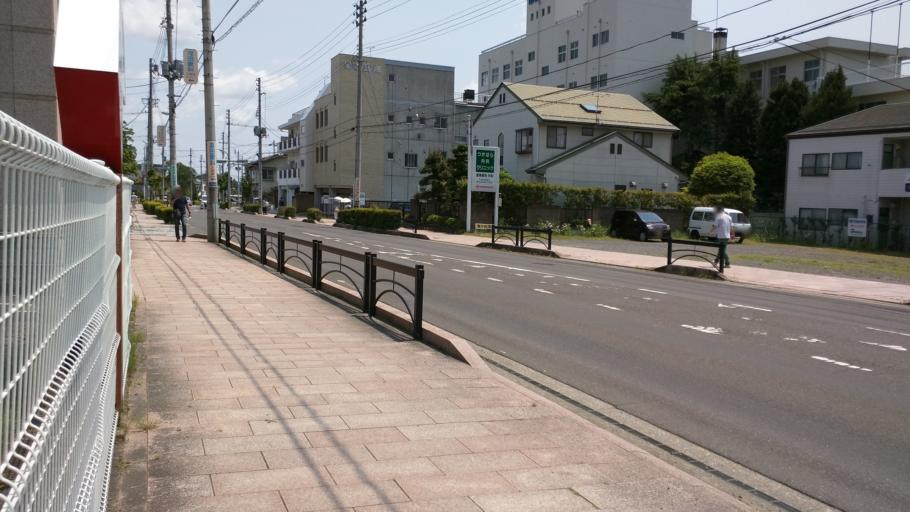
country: JP
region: Fukushima
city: Sukagawa
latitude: 37.1285
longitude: 140.2162
